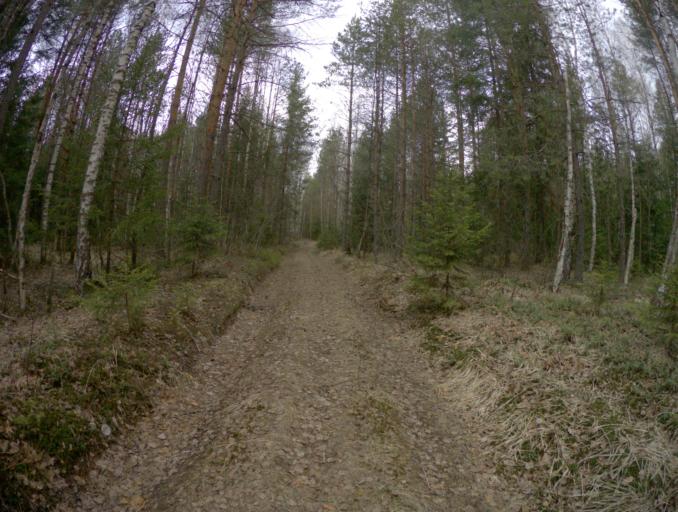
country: RU
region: Vladimir
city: Raduzhnyy
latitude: 55.9497
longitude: 40.2704
